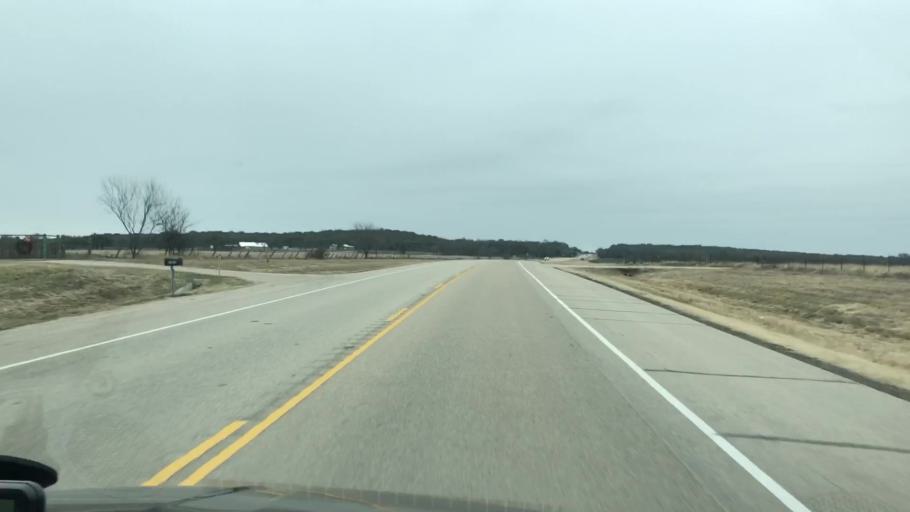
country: US
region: Texas
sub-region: Hamilton County
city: Hamilton
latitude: 31.7926
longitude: -98.1206
